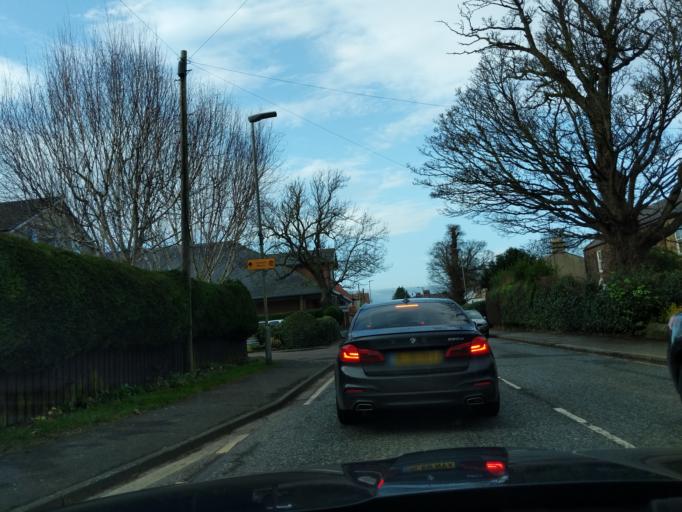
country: GB
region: England
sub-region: Northumberland
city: Ponteland
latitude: 55.0498
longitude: -1.7381
